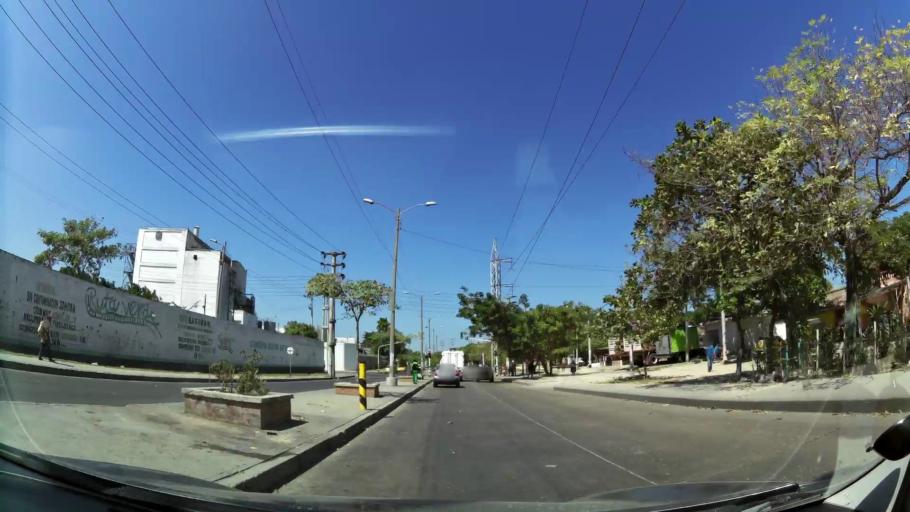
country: CO
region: Atlantico
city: Barranquilla
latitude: 10.9534
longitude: -74.7739
